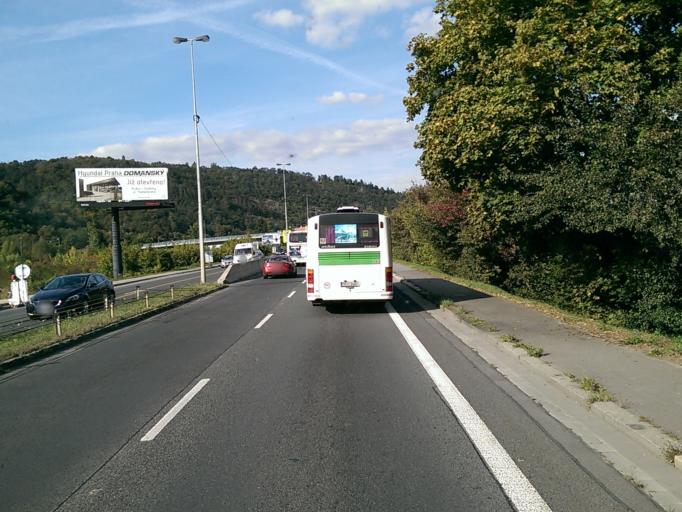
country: CZ
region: Praha
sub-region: Praha 12
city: Modrany
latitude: 50.0193
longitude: 14.3942
